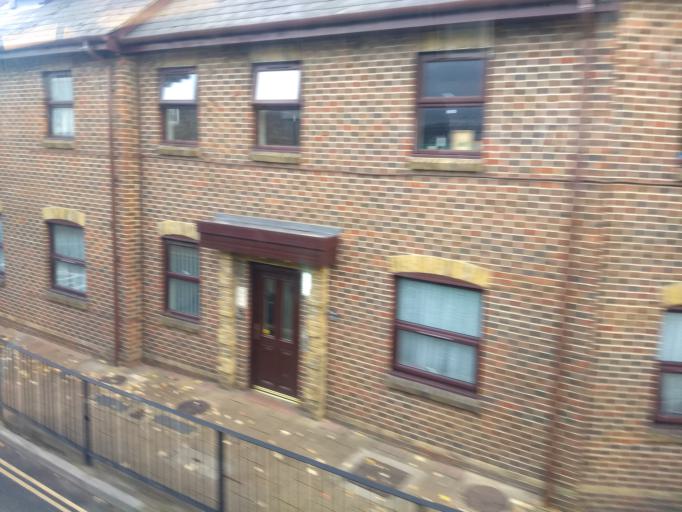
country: GB
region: England
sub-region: Isle of Wight
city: Newport
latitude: 50.6984
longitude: -1.2990
